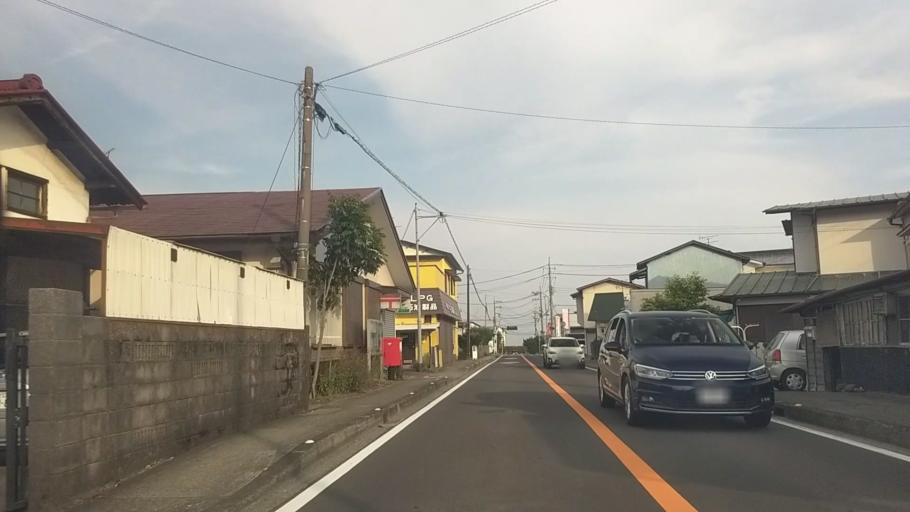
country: JP
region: Kanagawa
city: Odawara
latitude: 35.3525
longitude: 139.0929
